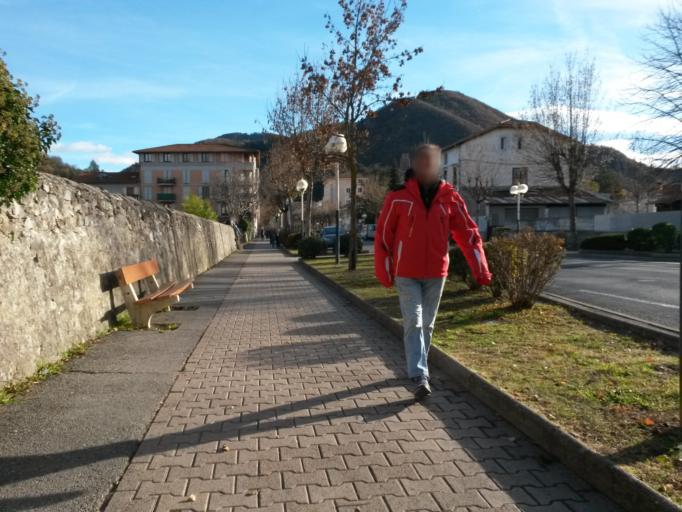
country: FR
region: Provence-Alpes-Cote d'Azur
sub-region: Departement des Alpes-de-Haute-Provence
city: Digne-les-Bains
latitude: 44.0963
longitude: 6.2347
